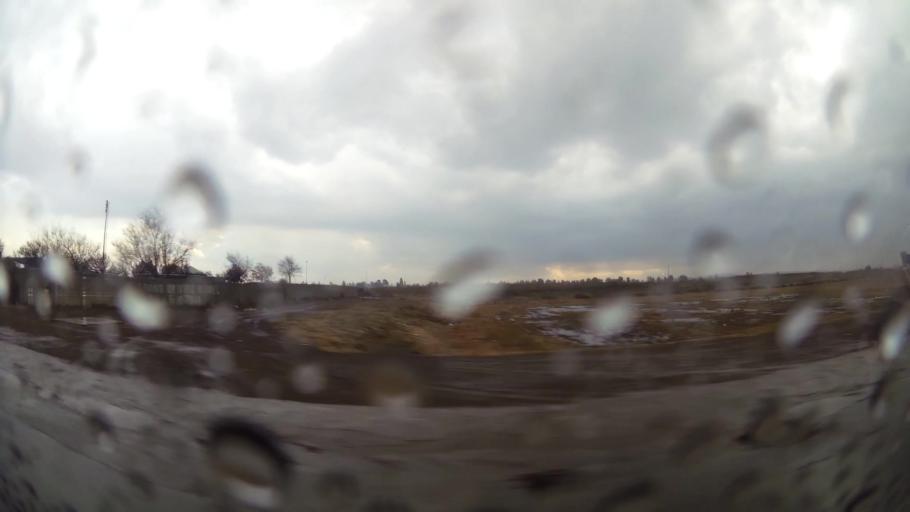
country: ZA
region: Gauteng
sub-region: Ekurhuleni Metropolitan Municipality
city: Germiston
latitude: -26.3514
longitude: 28.1330
